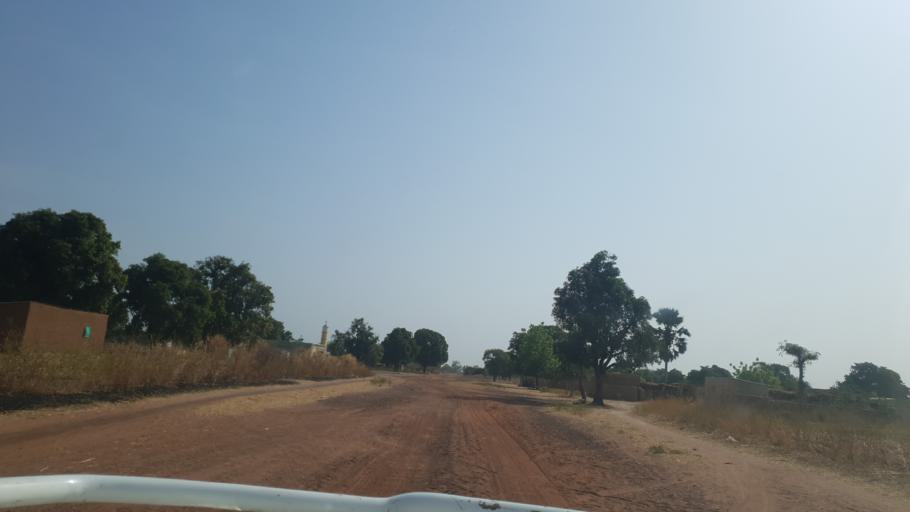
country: ML
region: Koulikoro
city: Dioila
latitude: 12.6688
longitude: -6.6760
